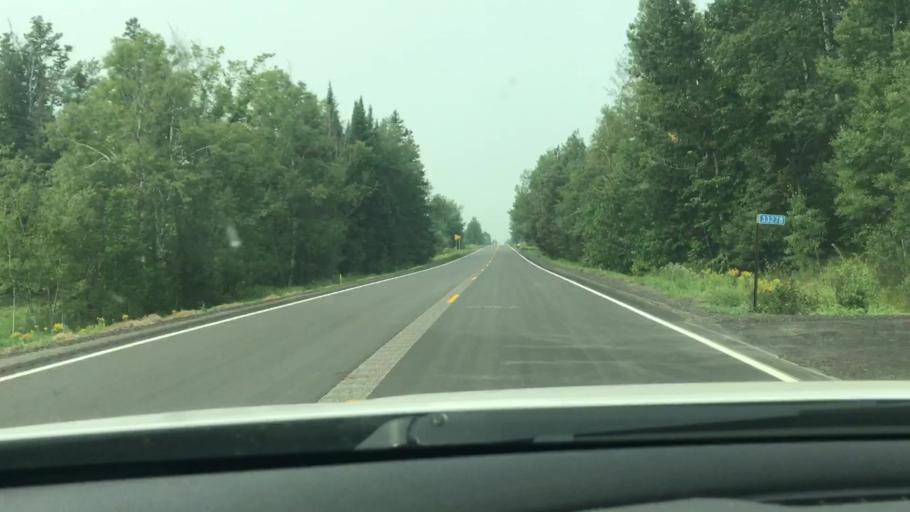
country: US
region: Minnesota
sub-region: Itasca County
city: Cohasset
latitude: 47.3579
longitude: -93.8565
